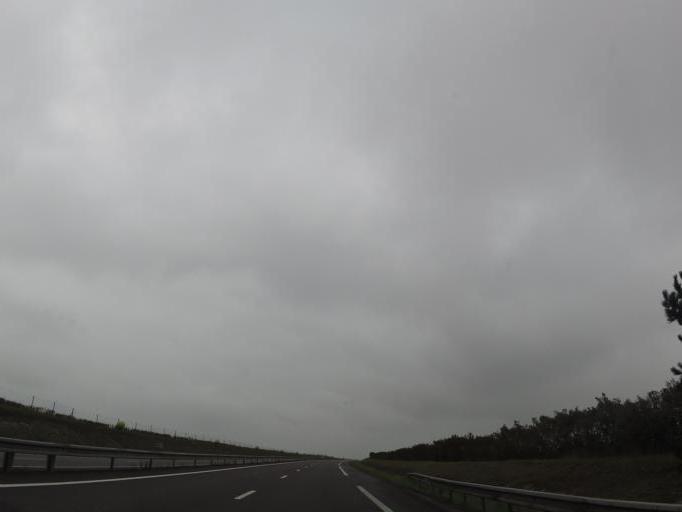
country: FR
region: Champagne-Ardenne
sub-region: Departement de la Marne
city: Sainte-Menehould
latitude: 49.0667
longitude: 4.7312
